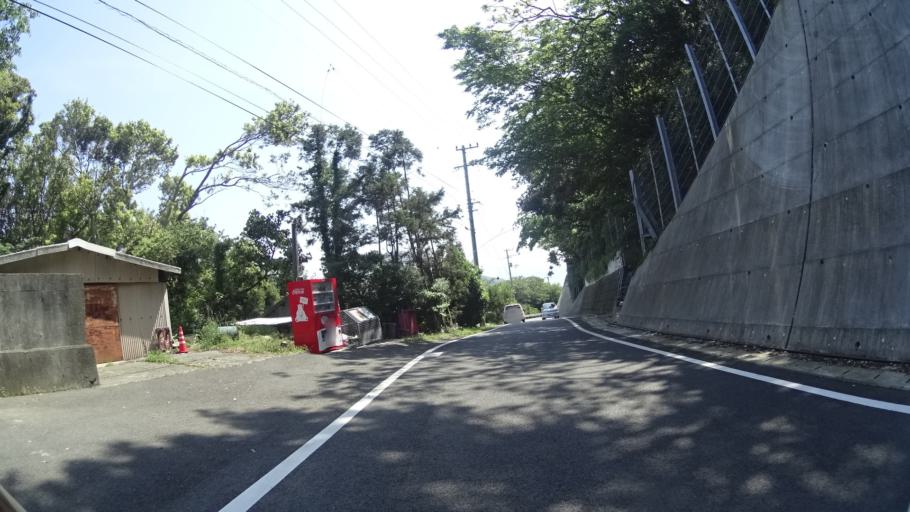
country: JP
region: Ehime
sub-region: Nishiuwa-gun
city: Ikata-cho
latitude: 33.3664
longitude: 132.0412
